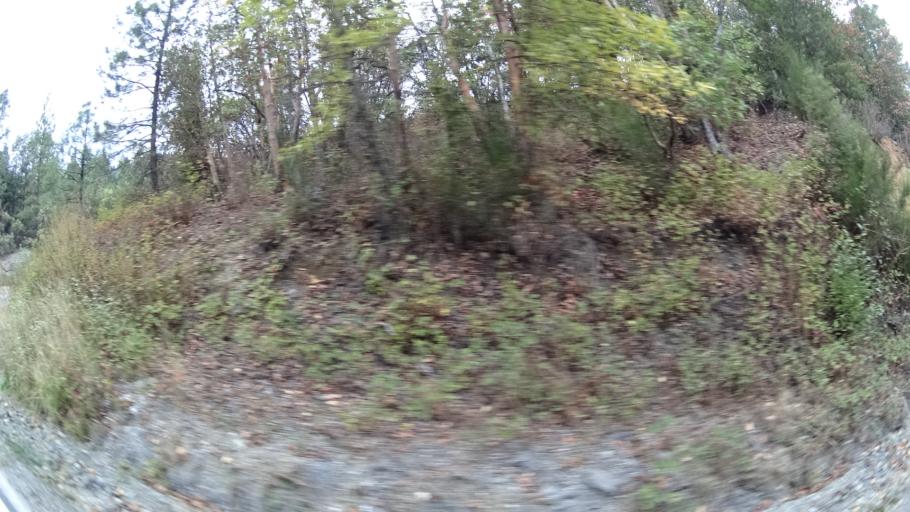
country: US
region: California
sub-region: Siskiyou County
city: Happy Camp
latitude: 41.7866
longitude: -123.3953
